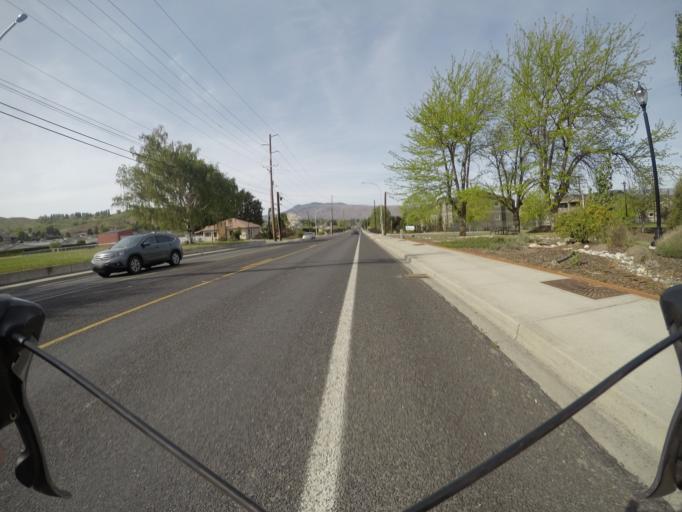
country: US
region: Washington
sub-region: Chelan County
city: West Wenatchee
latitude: 47.4393
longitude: -120.3461
